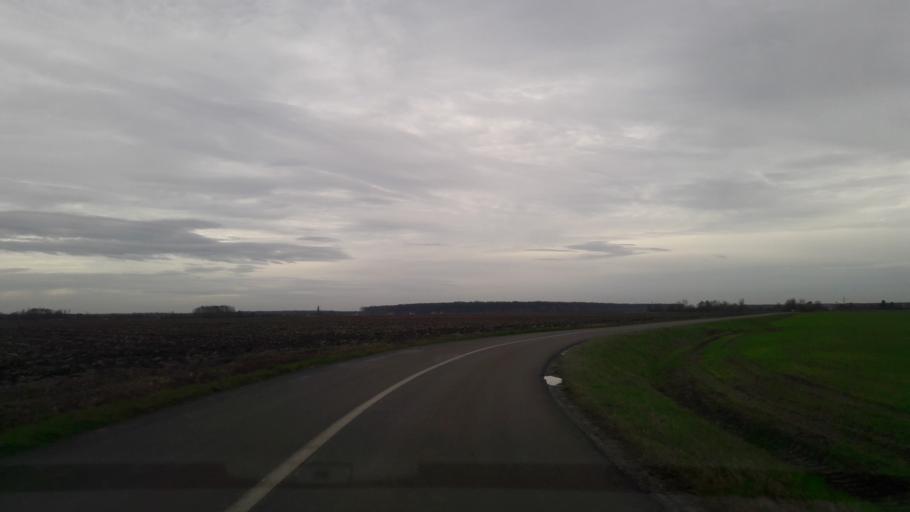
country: HR
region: Virovitick-Podravska
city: Zdenci
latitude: 45.6096
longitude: 18.0435
